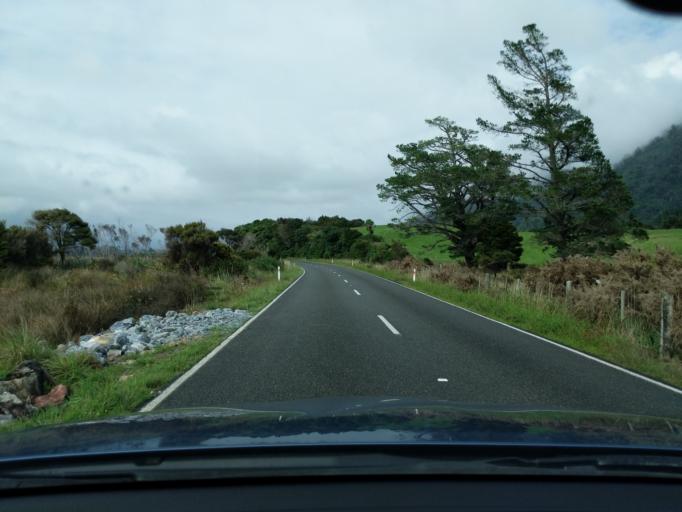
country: NZ
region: Tasman
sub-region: Tasman District
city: Takaka
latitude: -40.6488
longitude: 172.6564
